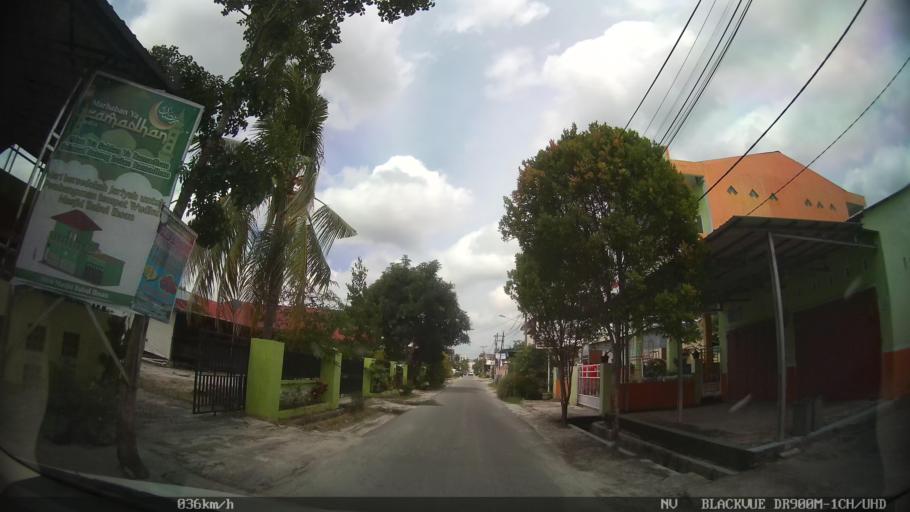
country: ID
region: North Sumatra
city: Percut
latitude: 3.5711
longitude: 98.8663
